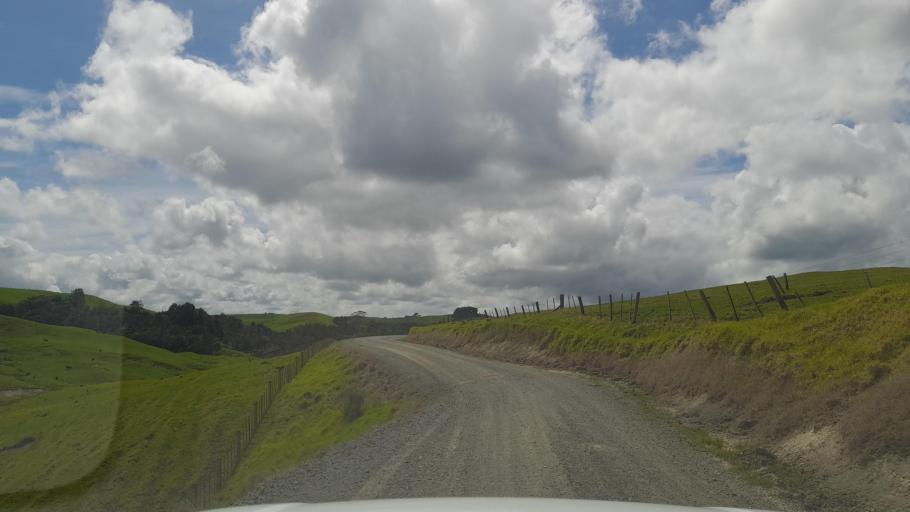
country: NZ
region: Auckland
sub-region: Auckland
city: Wellsford
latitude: -36.2137
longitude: 174.3237
